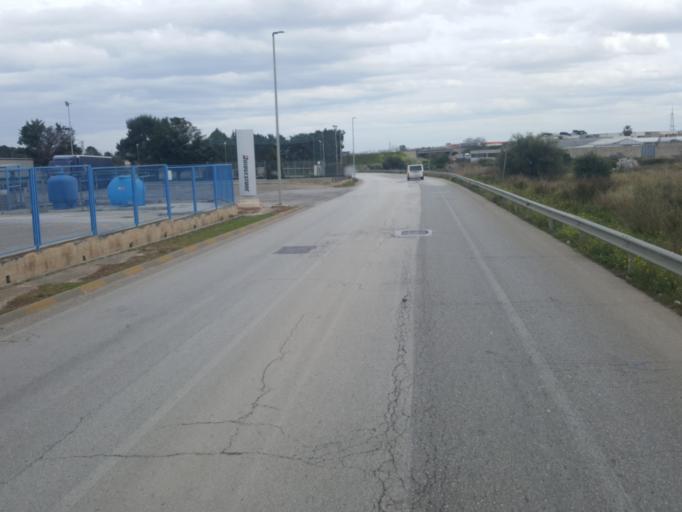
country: IT
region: Apulia
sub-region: Provincia di Bari
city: Modugno
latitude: 41.1029
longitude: 16.7997
